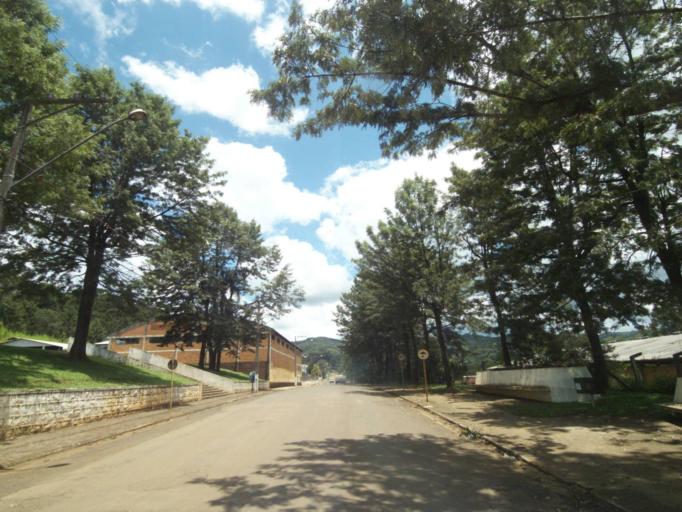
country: BR
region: Parana
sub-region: Uniao Da Vitoria
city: Uniao da Vitoria
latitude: -26.1626
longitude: -51.5531
